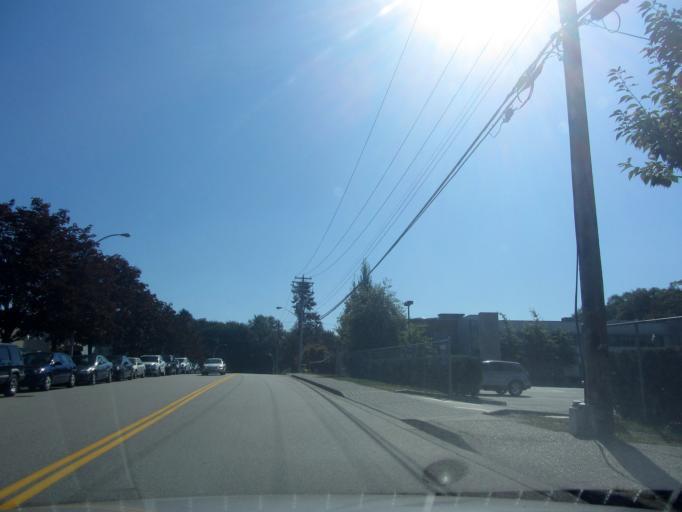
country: CA
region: British Columbia
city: Surrey
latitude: 49.1746
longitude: -122.8427
